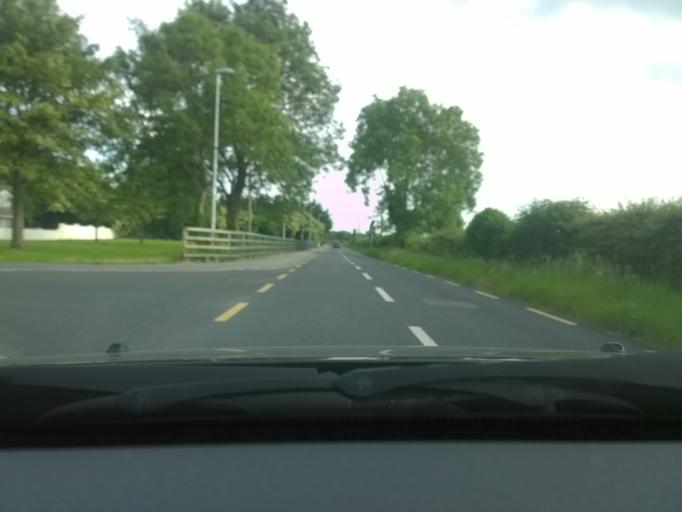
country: IE
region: Leinster
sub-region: Kildare
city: Kildare
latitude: 53.1672
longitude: -6.9130
